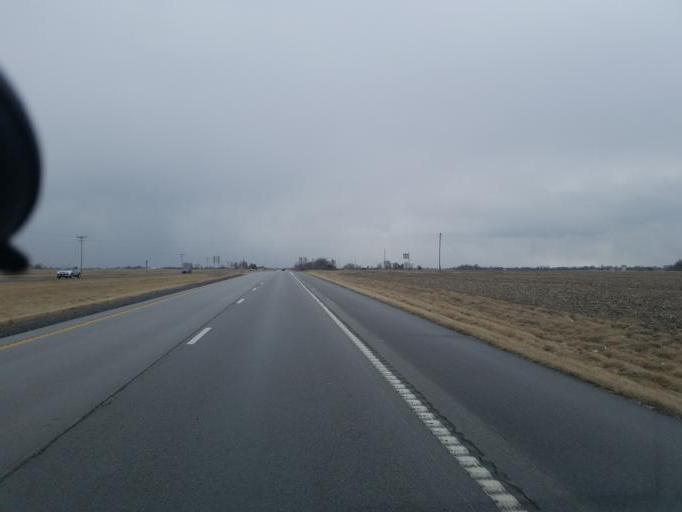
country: US
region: Missouri
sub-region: Macon County
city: Macon
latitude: 39.8405
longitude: -92.4798
